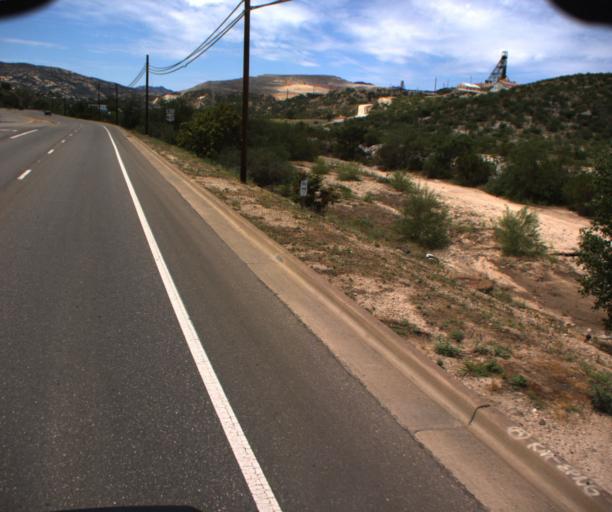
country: US
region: Arizona
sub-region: Gila County
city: Miami
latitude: 33.4040
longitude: -110.8609
